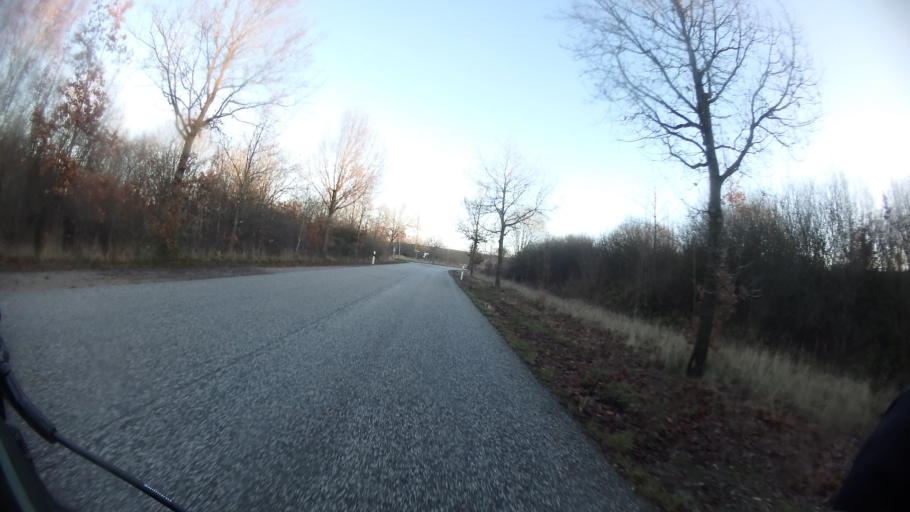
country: DE
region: Mecklenburg-Vorpommern
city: Selmsdorf
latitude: 53.9260
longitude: 10.8289
